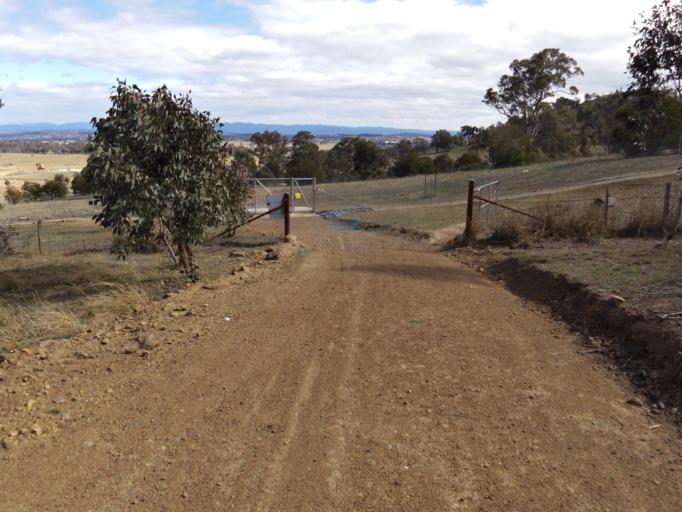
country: AU
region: Australian Capital Territory
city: Kaleen
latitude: -35.2101
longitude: 149.1827
